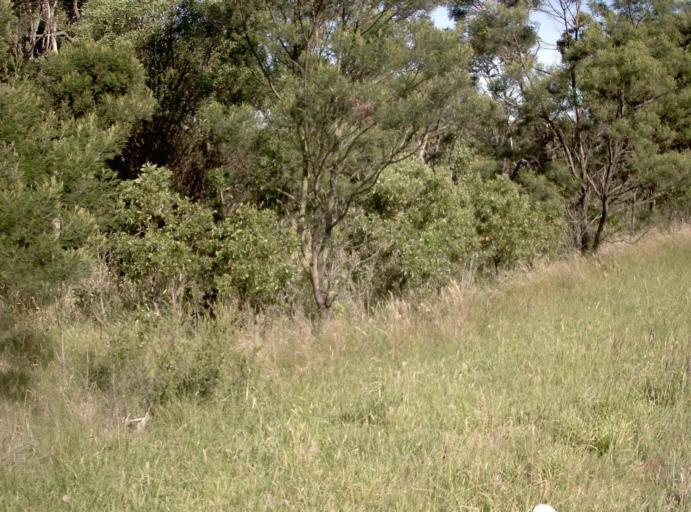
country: AU
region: Victoria
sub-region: Latrobe
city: Traralgon
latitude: -38.6226
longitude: 146.6731
